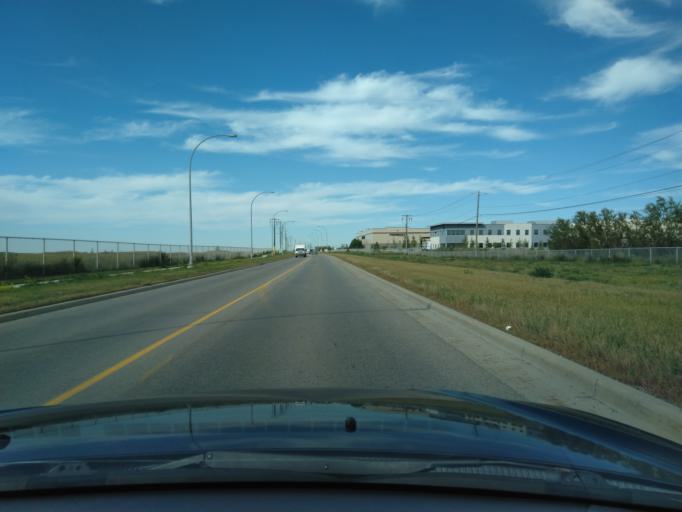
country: CA
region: Alberta
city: Calgary
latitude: 51.1064
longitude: -113.9822
